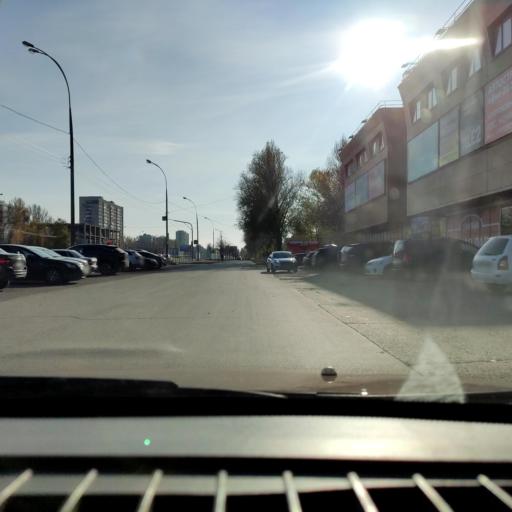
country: RU
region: Samara
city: Tol'yatti
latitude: 53.5338
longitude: 49.2824
